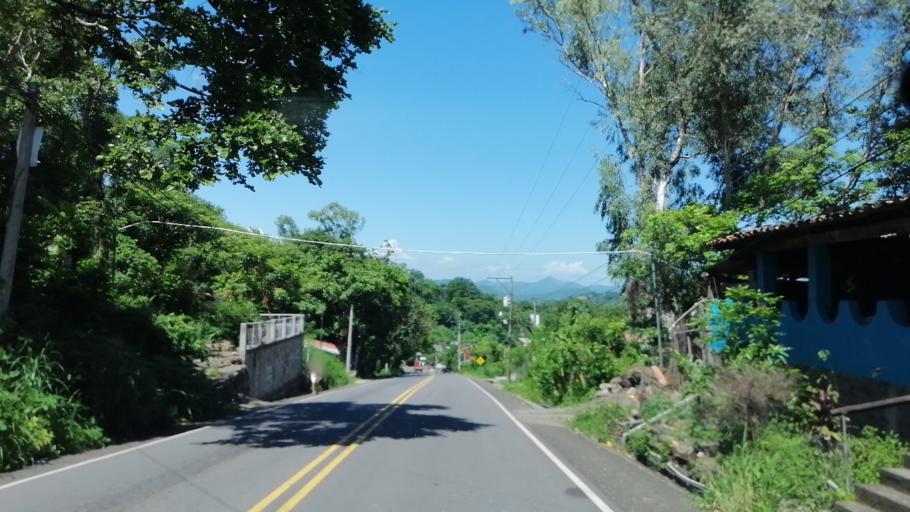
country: SV
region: Morazan
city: Cacaopera
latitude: 13.8071
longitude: -88.1479
